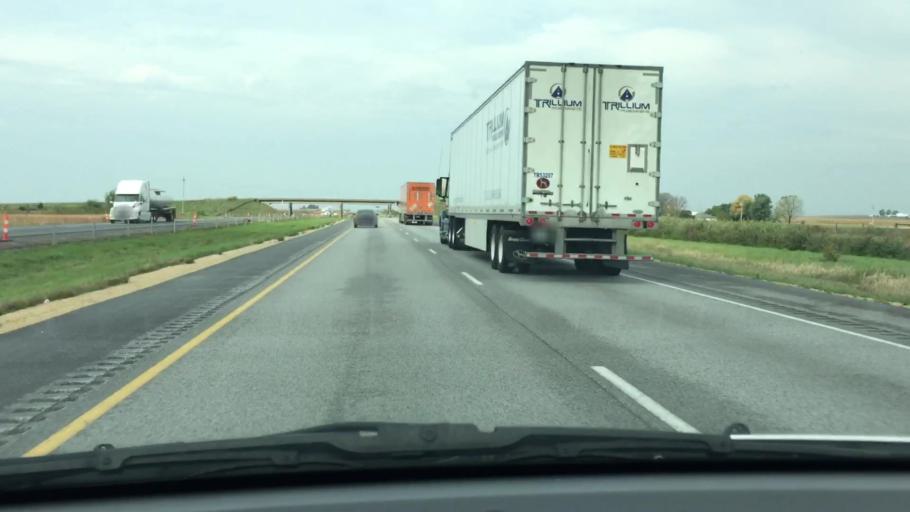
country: US
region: Iowa
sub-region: Scott County
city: Walcott
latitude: 41.6079
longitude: -90.7399
